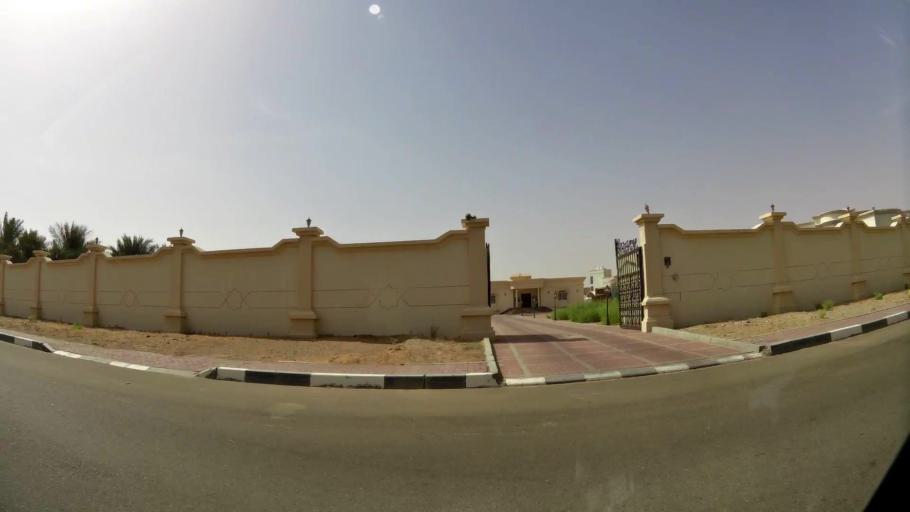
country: AE
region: Abu Dhabi
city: Al Ain
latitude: 24.1611
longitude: 55.6813
